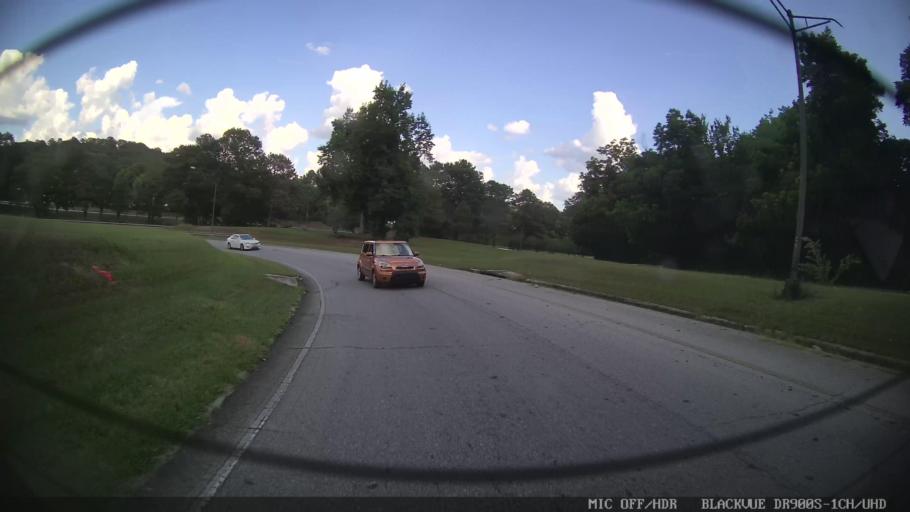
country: US
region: Georgia
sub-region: Floyd County
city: Rome
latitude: 34.2366
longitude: -85.1644
